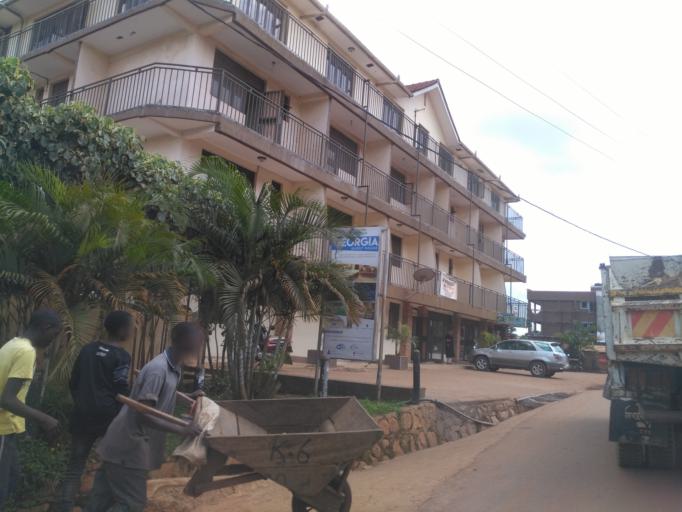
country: UG
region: Central Region
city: Kampala Central Division
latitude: 0.3603
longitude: 32.5838
